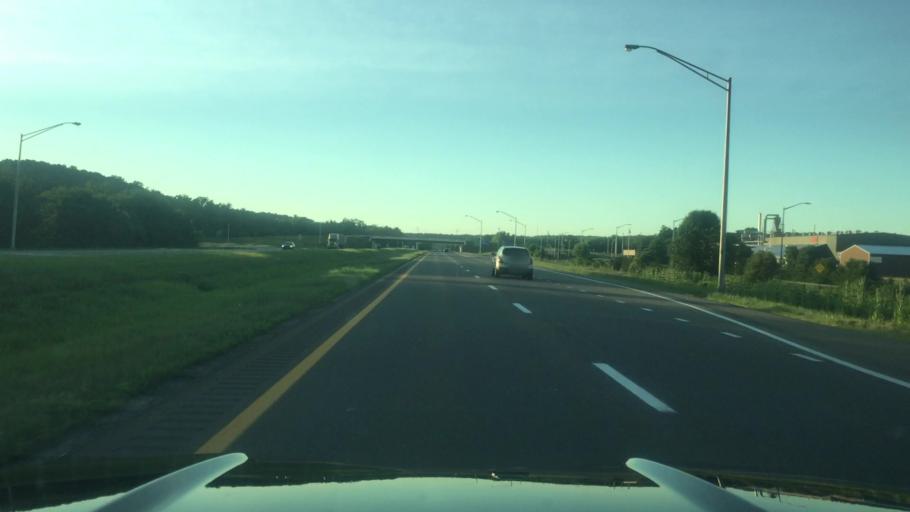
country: US
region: Ohio
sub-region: Tuscarawas County
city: Dover
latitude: 40.5450
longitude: -81.5014
